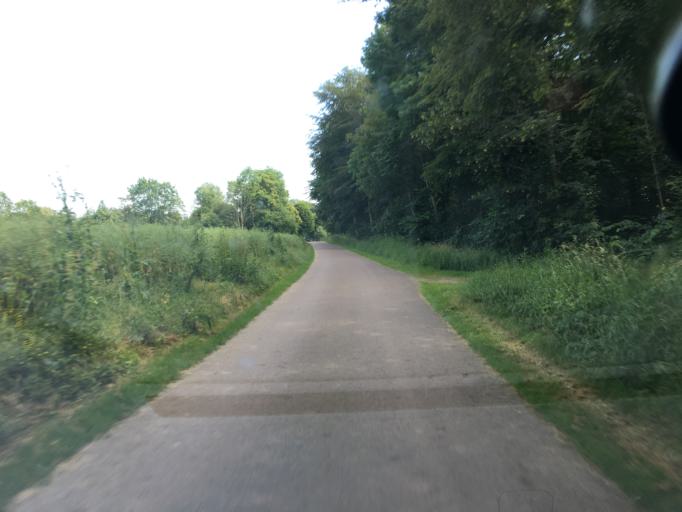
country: DK
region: South Denmark
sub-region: Sonderborg Kommune
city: Dybbol
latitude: 54.9516
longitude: 9.7455
